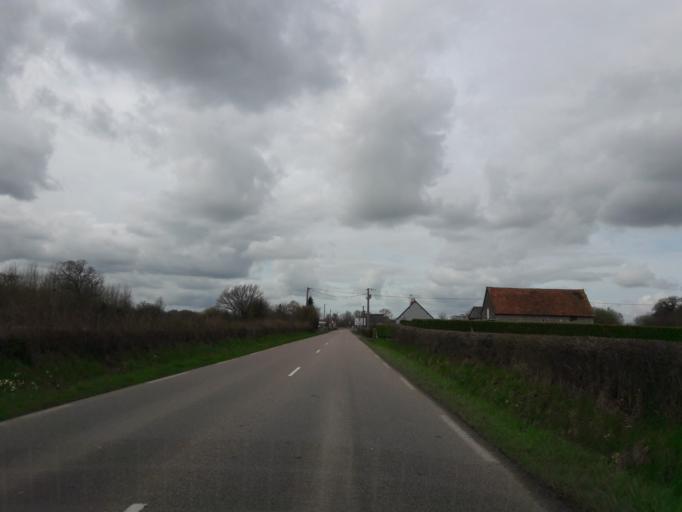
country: FR
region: Lower Normandy
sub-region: Departement de la Manche
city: La Meauffe
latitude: 49.2190
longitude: -1.1305
